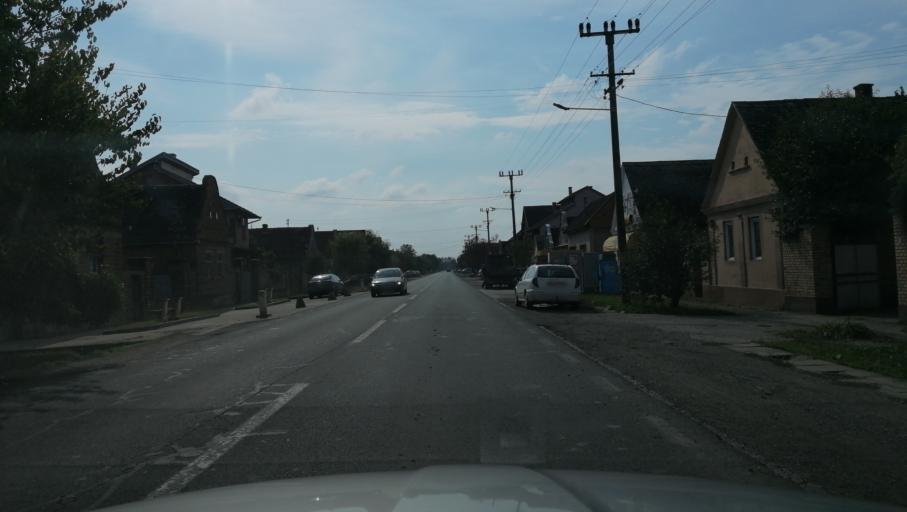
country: RS
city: Ravnje
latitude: 45.0225
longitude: 19.4031
